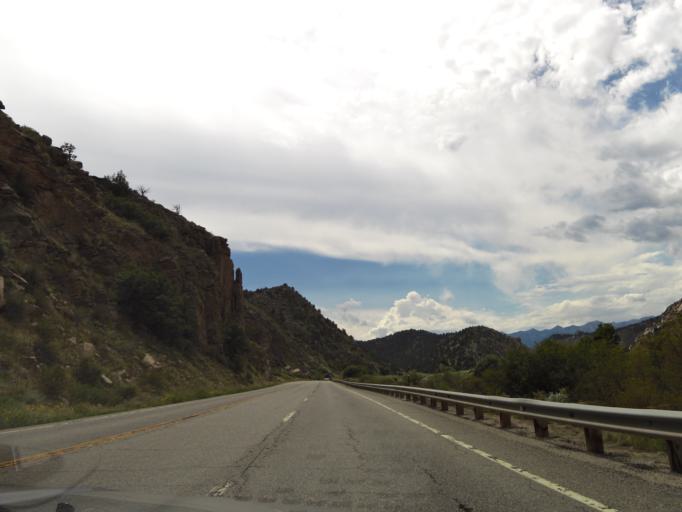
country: US
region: Colorado
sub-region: Custer County
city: Westcliffe
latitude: 38.3946
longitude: -105.6362
